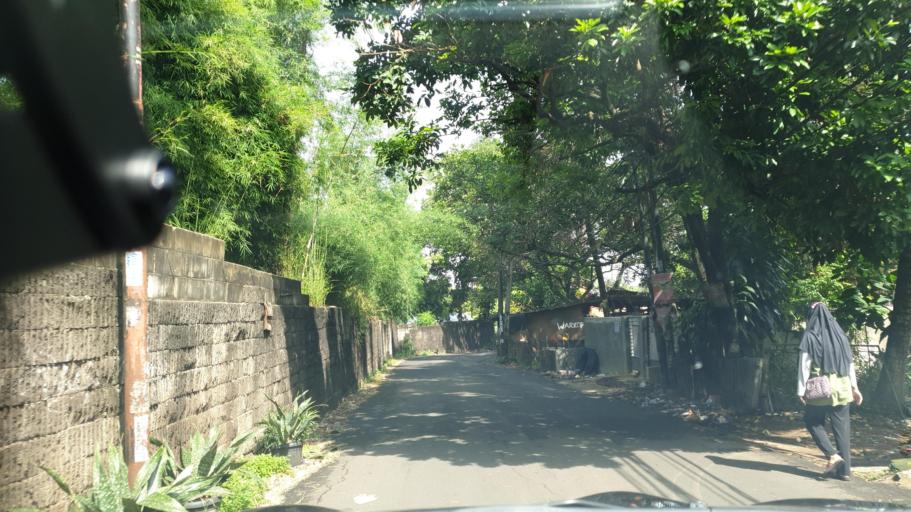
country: ID
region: West Java
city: Pamulang
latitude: -6.3022
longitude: 106.7655
